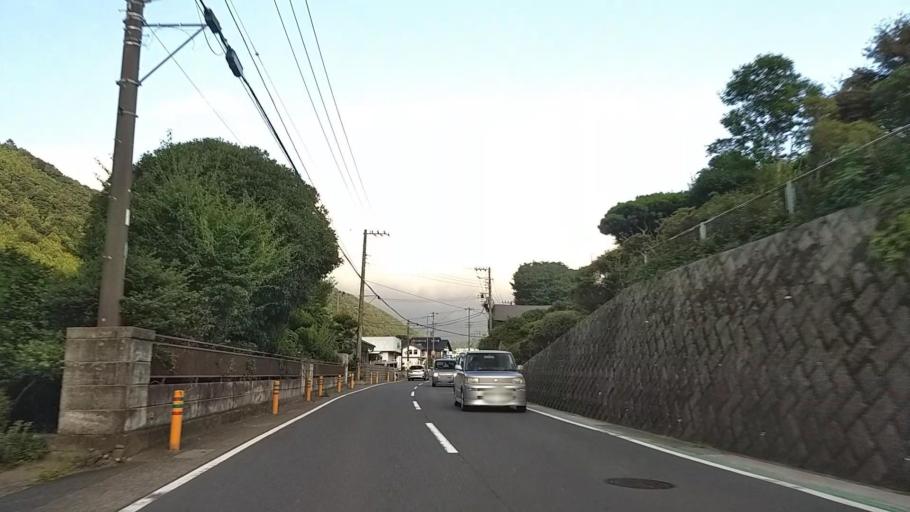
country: JP
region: Kanagawa
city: Atsugi
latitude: 35.4838
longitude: 139.2749
